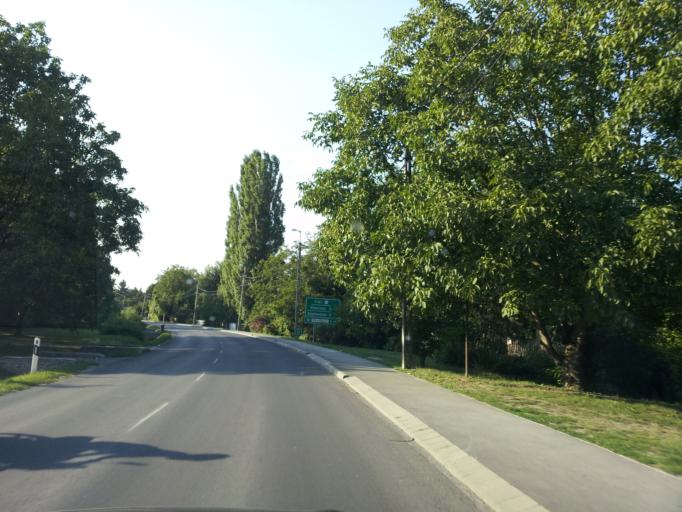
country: HU
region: Pest
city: Tahitotfalu
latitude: 47.7478
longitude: 19.0819
